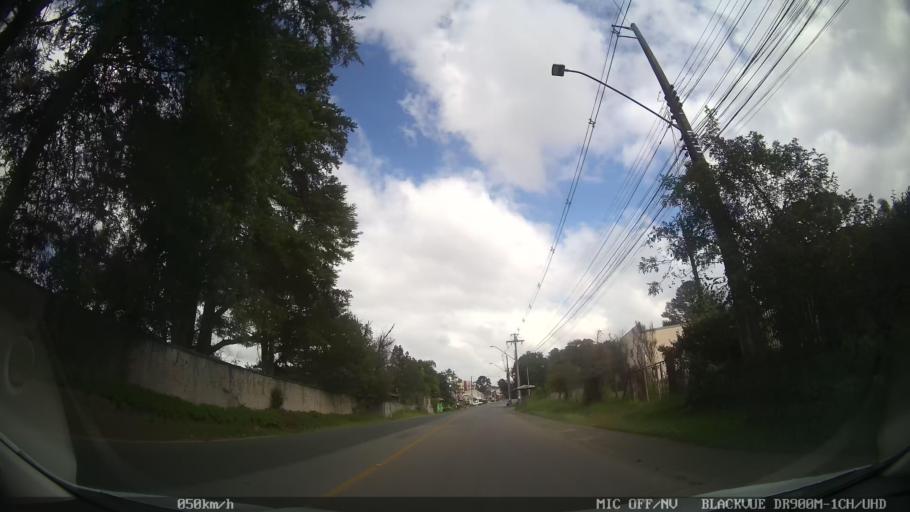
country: BR
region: Parana
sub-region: Pinhais
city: Pinhais
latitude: -25.3706
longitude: -49.2167
